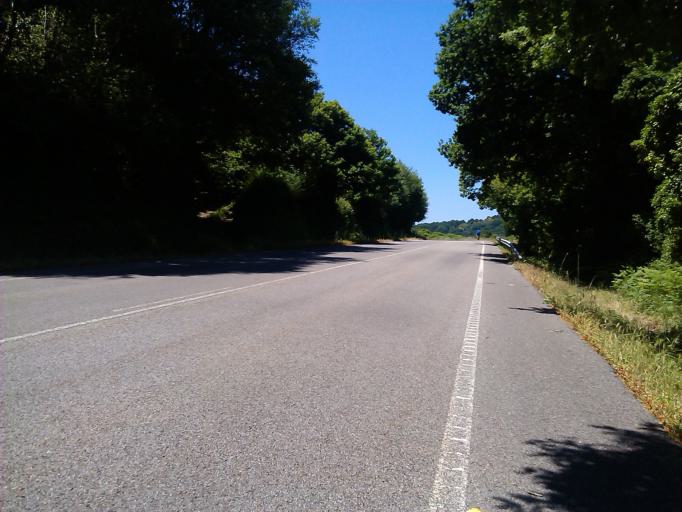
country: ES
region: Galicia
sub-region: Provincia de Lugo
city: Samos
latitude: 42.7385
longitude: -7.3020
